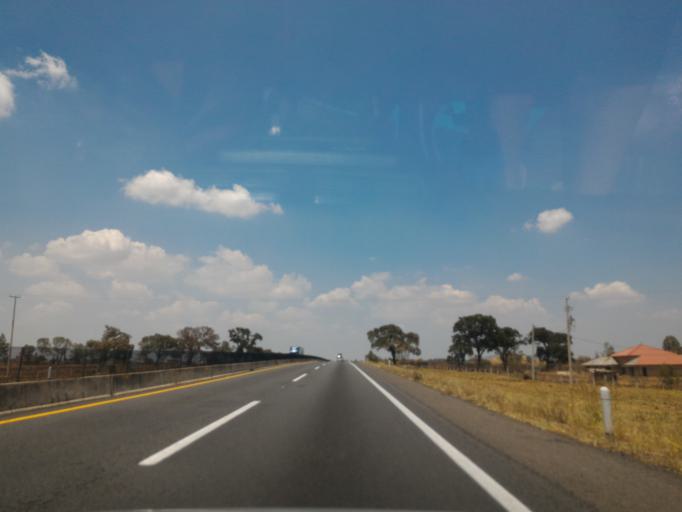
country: MX
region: Jalisco
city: Tepatitlan de Morelos
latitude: 20.8729
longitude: -102.7466
